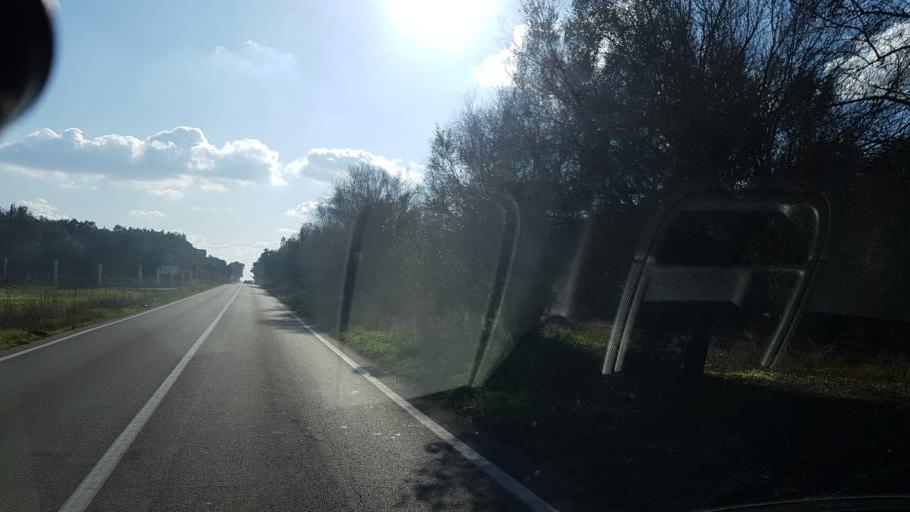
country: IT
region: Apulia
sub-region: Provincia di Lecce
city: Campi Salentina
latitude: 40.4172
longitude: 18.0244
